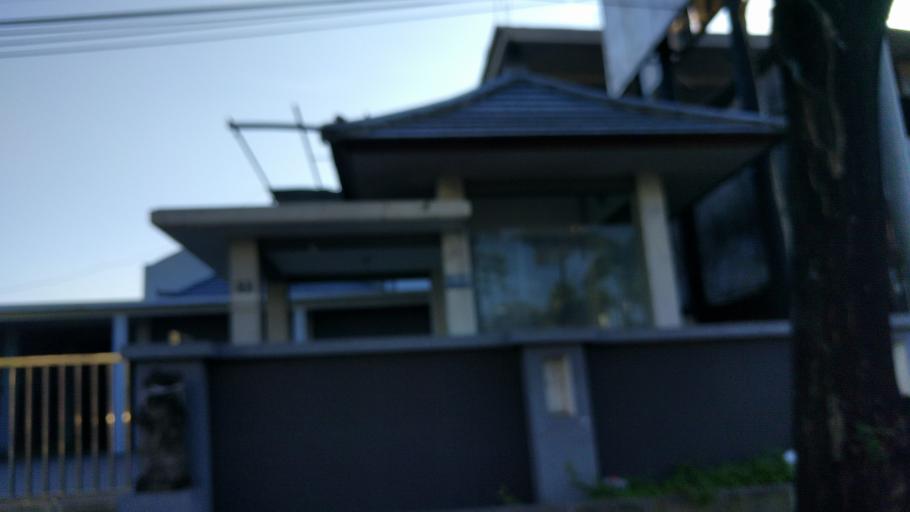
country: ID
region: Bali
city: Kuta
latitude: -8.7036
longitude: 115.1810
